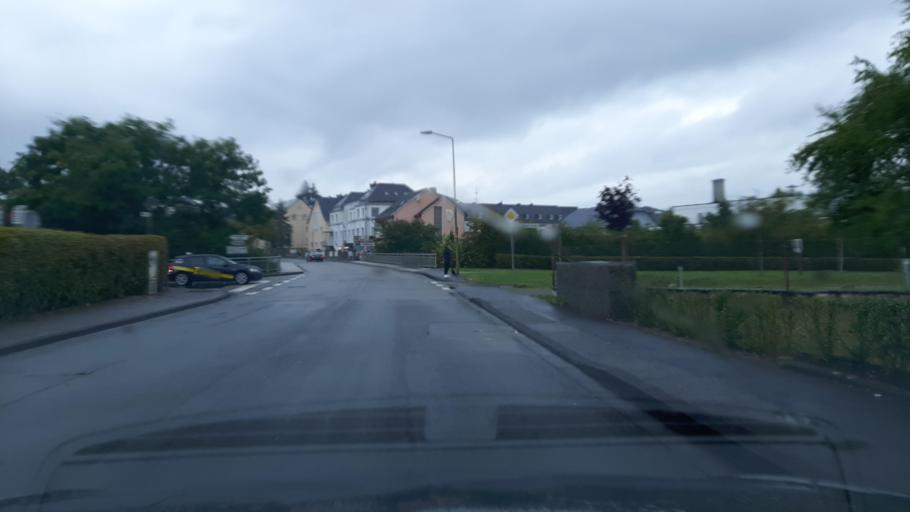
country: DE
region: Rheinland-Pfalz
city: Bitburg
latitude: 49.9671
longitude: 6.5290
